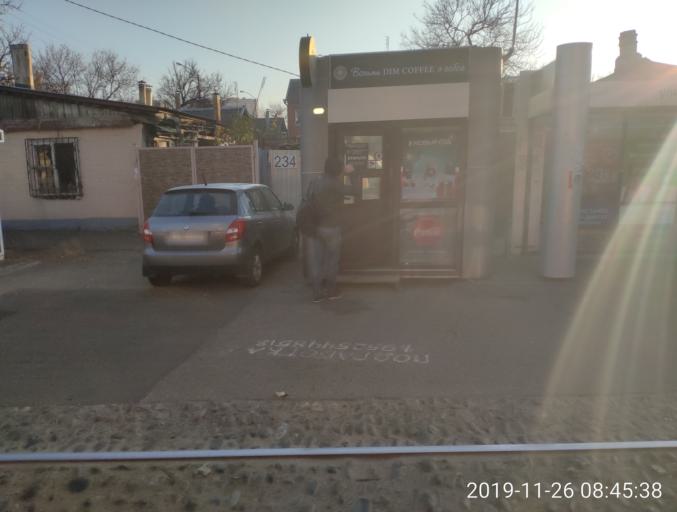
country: RU
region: Krasnodarskiy
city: Krasnodar
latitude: 45.0414
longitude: 38.9804
